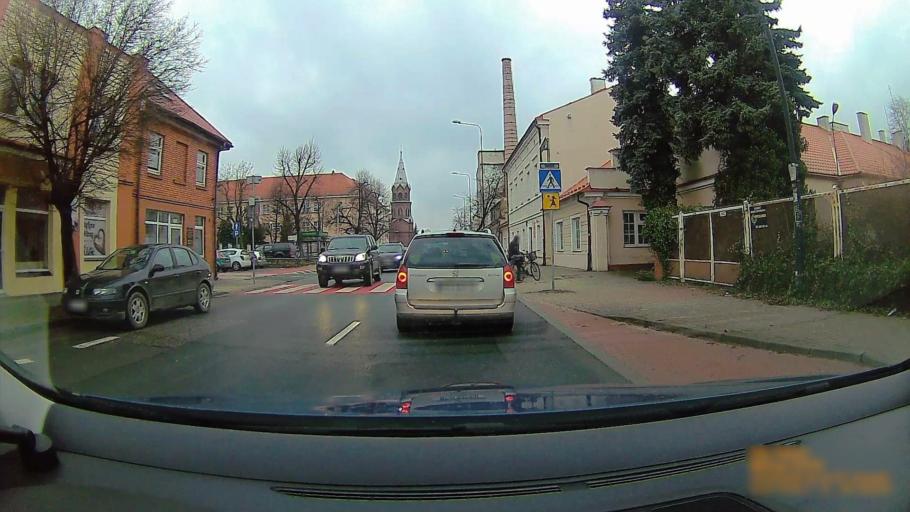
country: PL
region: Greater Poland Voivodeship
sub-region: Konin
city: Konin
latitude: 52.2045
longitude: 18.2562
